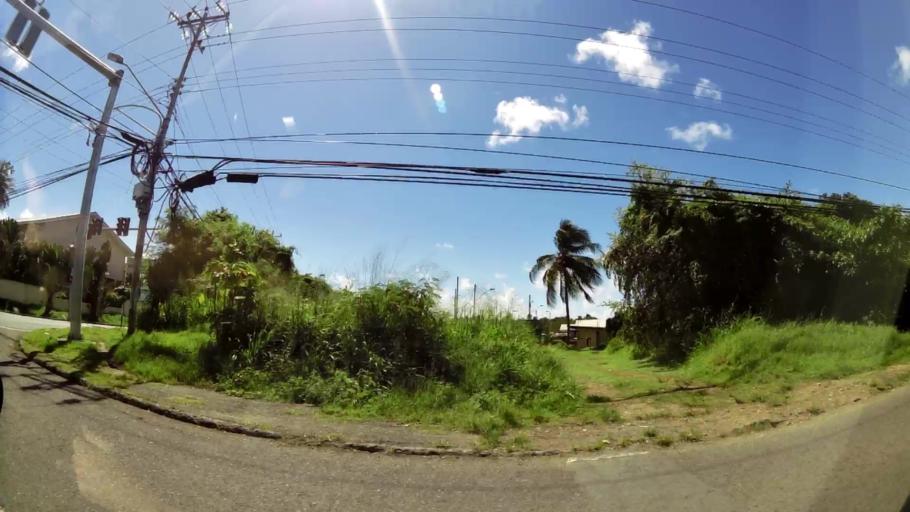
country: TT
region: Tobago
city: Scarborough
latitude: 11.1818
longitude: -60.8006
